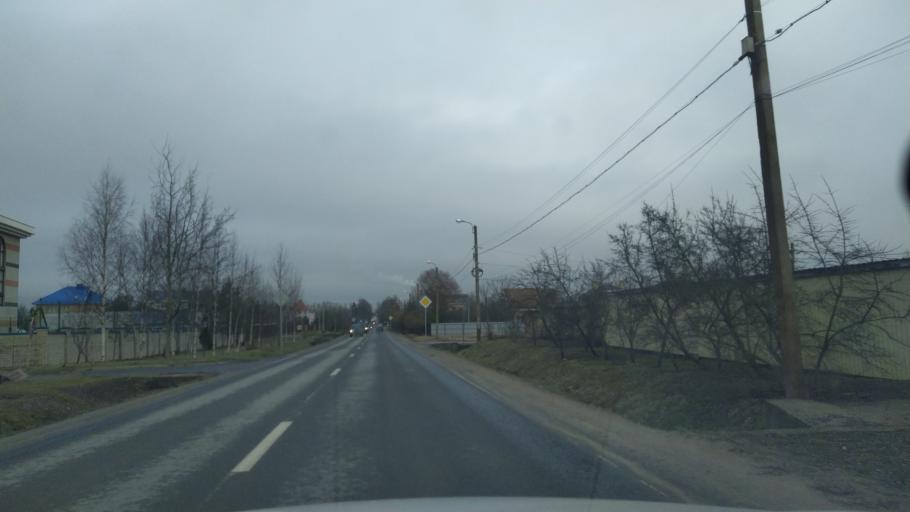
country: RU
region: St.-Petersburg
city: Aleksandrovskaya
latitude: 59.7232
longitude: 30.3476
